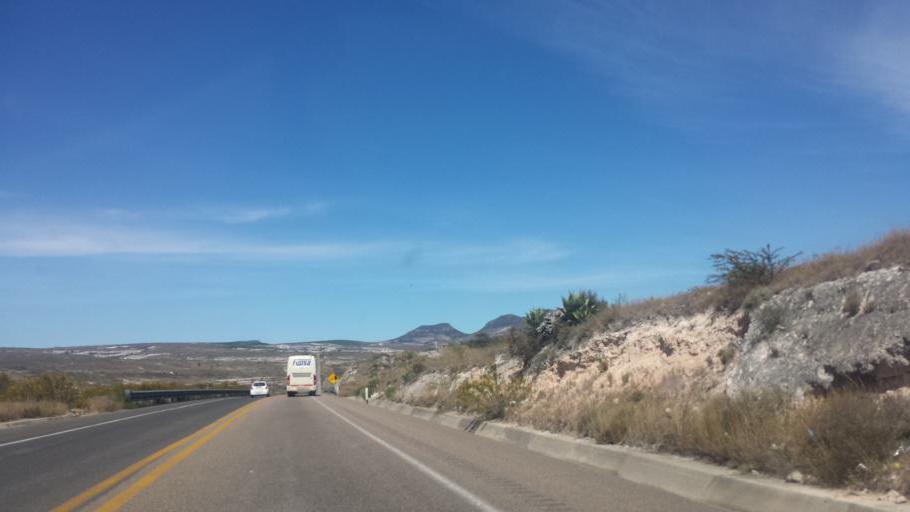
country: MX
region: Oaxaca
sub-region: Villa Tejupam de la Union
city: Villa Tejupam de la Union
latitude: 17.7798
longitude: -97.3610
